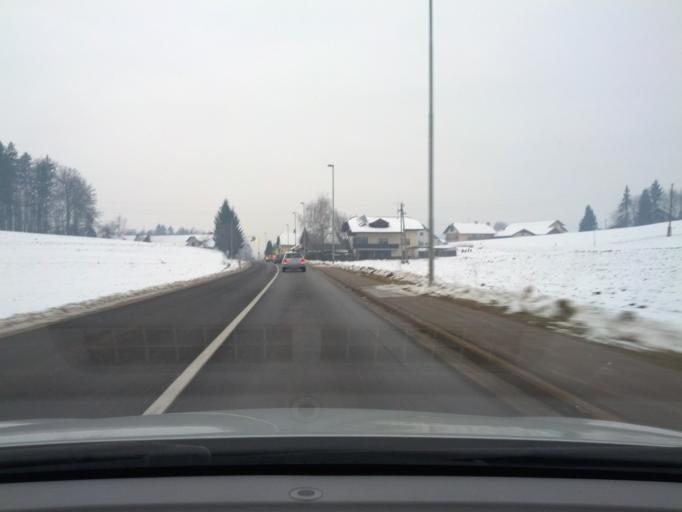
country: SI
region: Lukovica
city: Lukovica pri Domzalah
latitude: 46.1429
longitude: 14.6686
